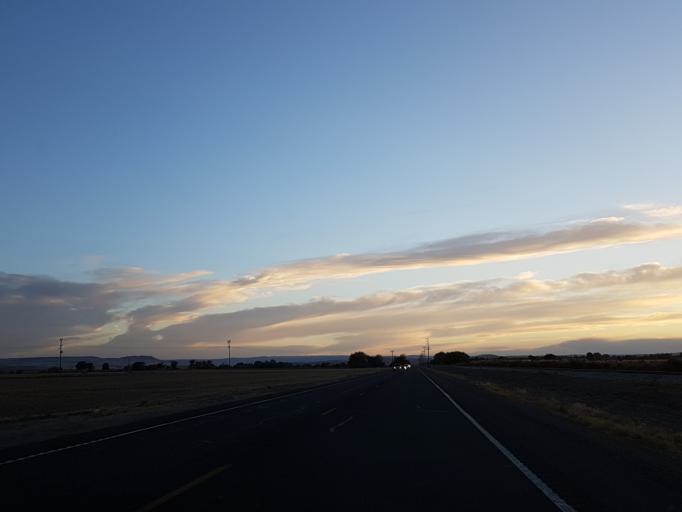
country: US
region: Oregon
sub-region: Malheur County
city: Vale
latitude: 43.9775
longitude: -117.2590
